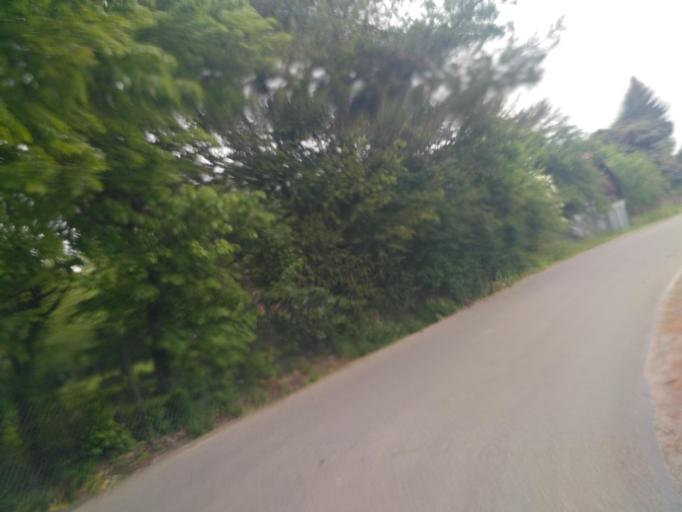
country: PL
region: Subcarpathian Voivodeship
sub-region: Powiat krosnienski
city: Chorkowka
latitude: 49.6664
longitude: 21.7091
